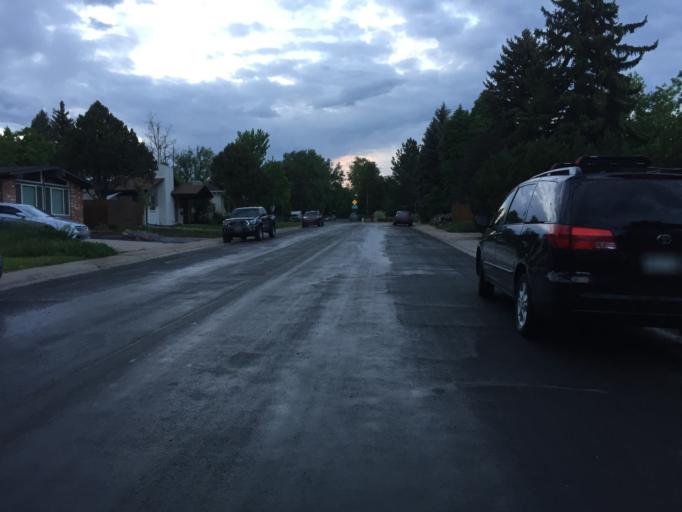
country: US
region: Colorado
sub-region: Boulder County
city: Boulder
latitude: 40.0294
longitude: -105.2803
